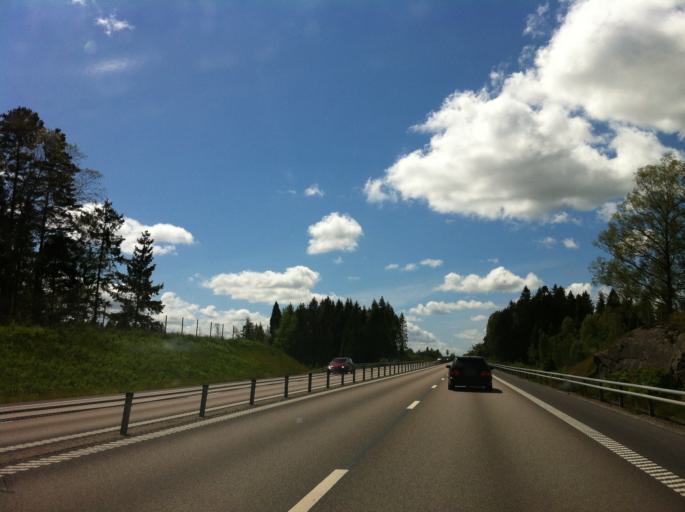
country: SE
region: Vaestra Goetaland
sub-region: Trollhattan
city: Sjuntorp
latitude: 58.2413
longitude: 12.2461
